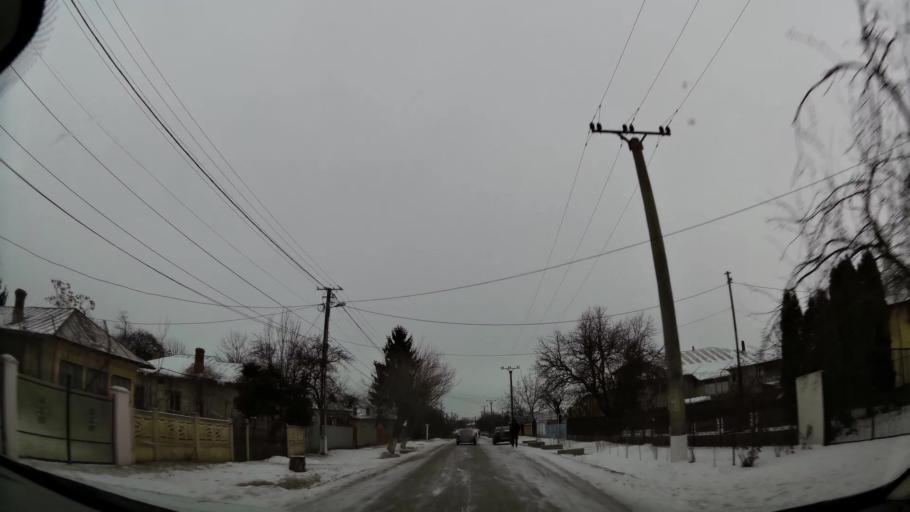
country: RO
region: Prahova
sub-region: Comuna Poenarii-Burchi
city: Ologeni
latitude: 44.7329
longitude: 25.9497
